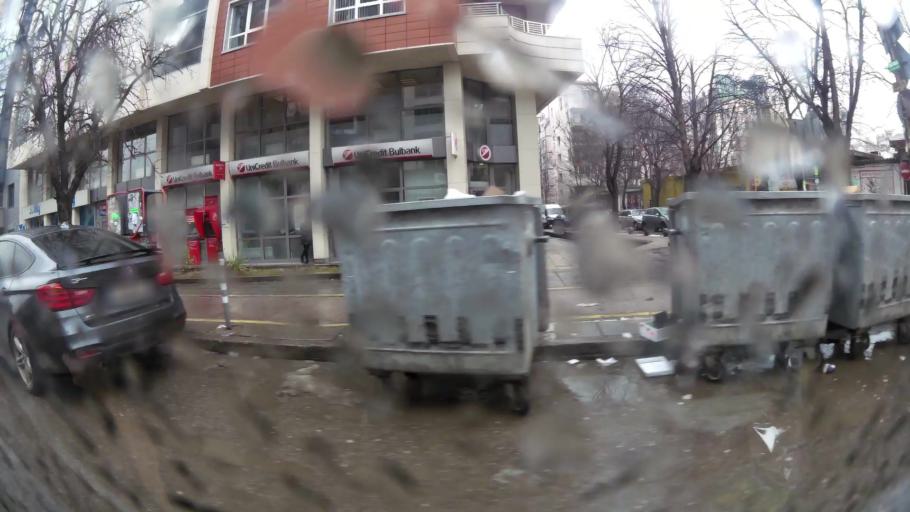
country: BG
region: Sofia-Capital
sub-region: Stolichna Obshtina
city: Sofia
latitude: 42.6712
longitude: 23.2954
